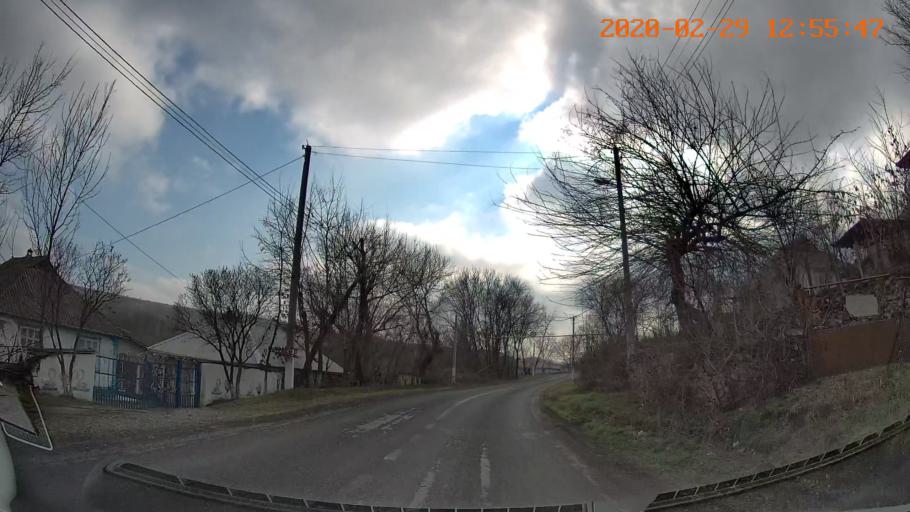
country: MD
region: Telenesti
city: Camenca
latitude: 48.0919
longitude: 28.7244
